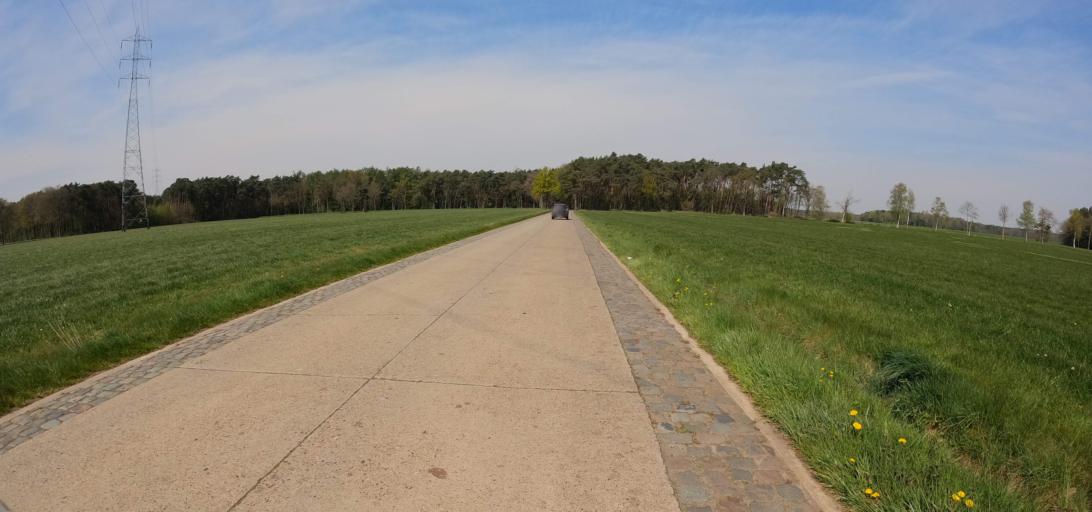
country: BE
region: Flanders
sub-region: Provincie Antwerpen
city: Vorselaar
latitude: 51.2339
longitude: 4.7745
